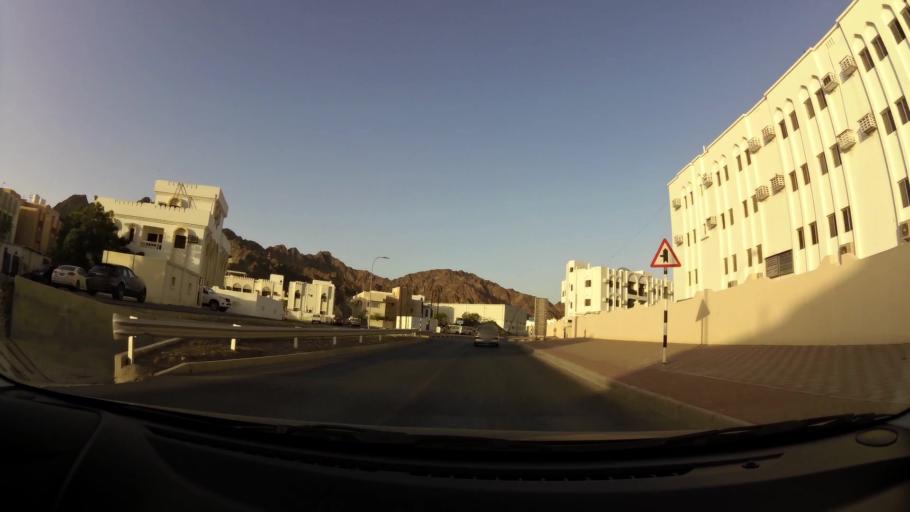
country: OM
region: Muhafazat Masqat
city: Muscat
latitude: 23.5715
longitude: 58.5726
